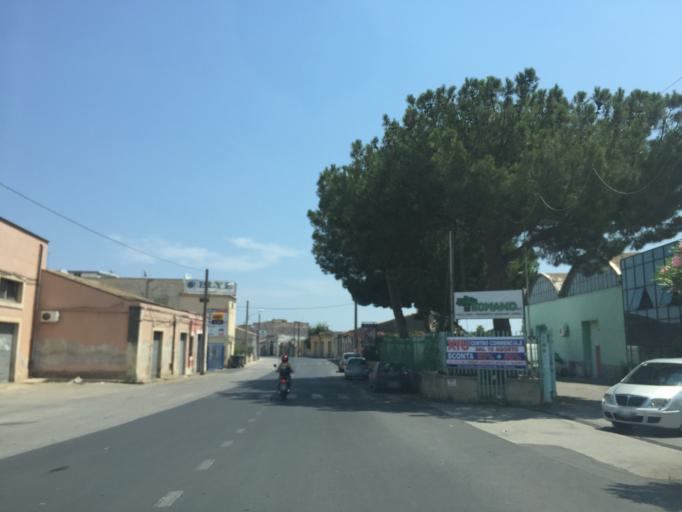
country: IT
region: Sicily
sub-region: Provincia di Siracusa
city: Siracusa
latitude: 37.0701
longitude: 15.2723
